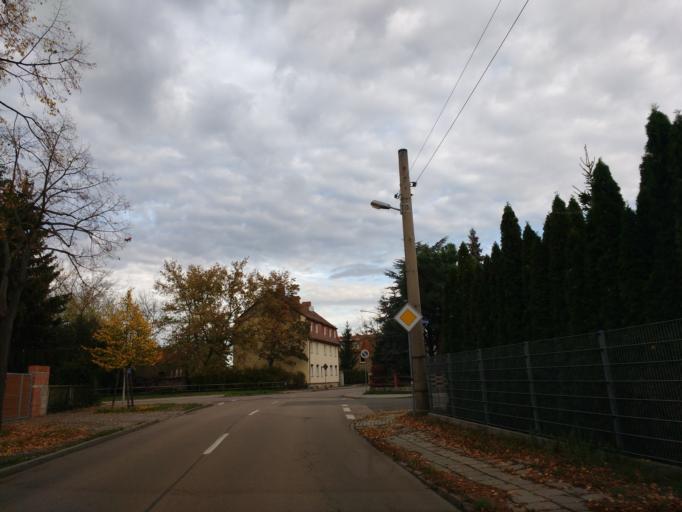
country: DE
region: Saxony-Anhalt
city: Dolbau
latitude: 51.4753
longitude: 12.0301
